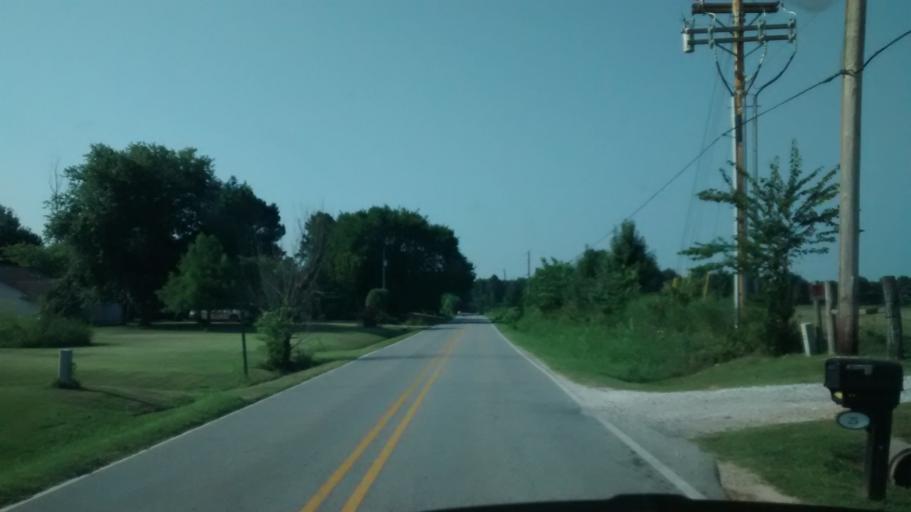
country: US
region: Arkansas
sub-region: Washington County
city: Farmington
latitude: 36.0650
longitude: -94.2535
